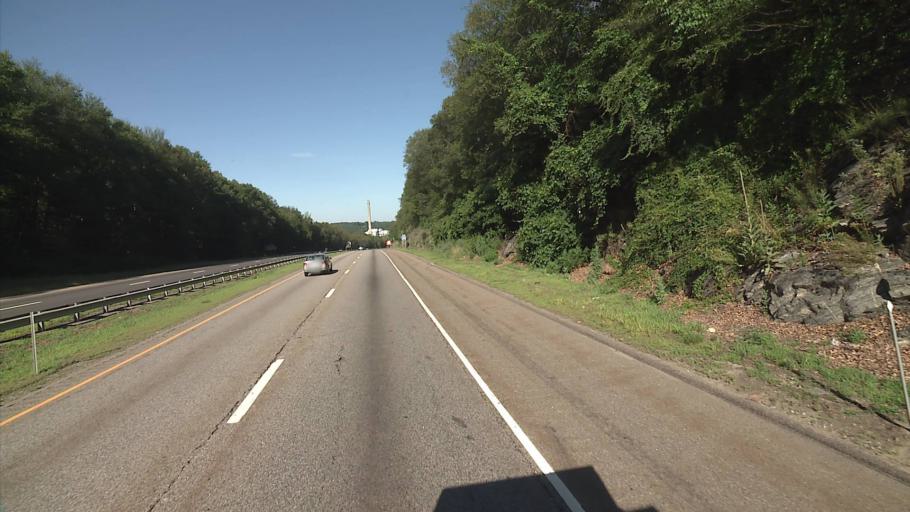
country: US
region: Connecticut
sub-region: New London County
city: Lisbon
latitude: 41.5869
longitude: -72.0311
